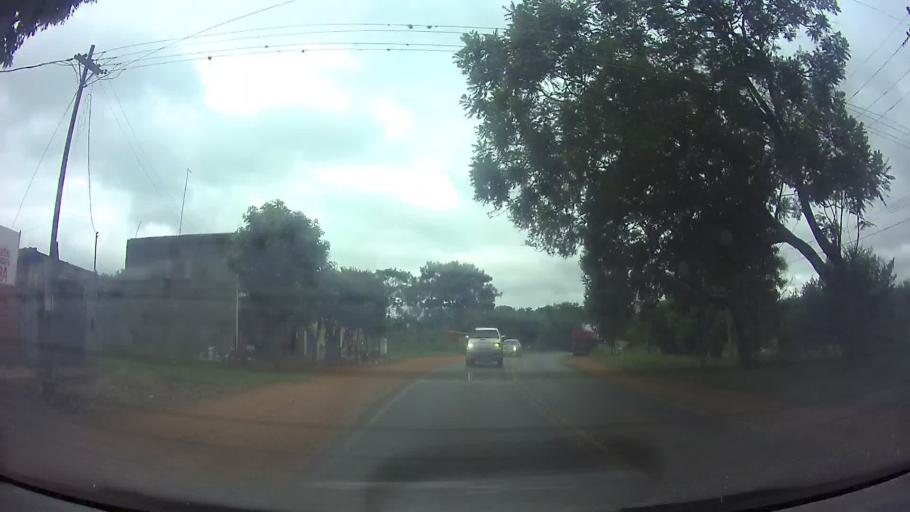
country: PY
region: Central
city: Guarambare
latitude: -25.5351
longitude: -57.5008
